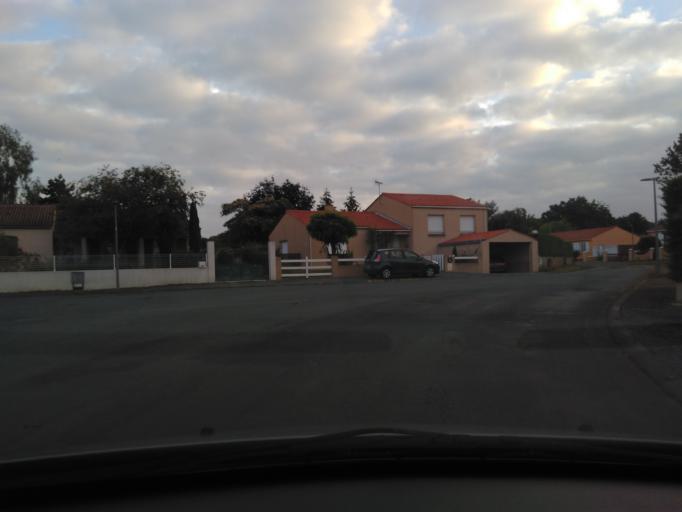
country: FR
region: Pays de la Loire
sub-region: Departement de la Vendee
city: Dompierre-sur-Yon
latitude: 46.7340
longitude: -1.3964
